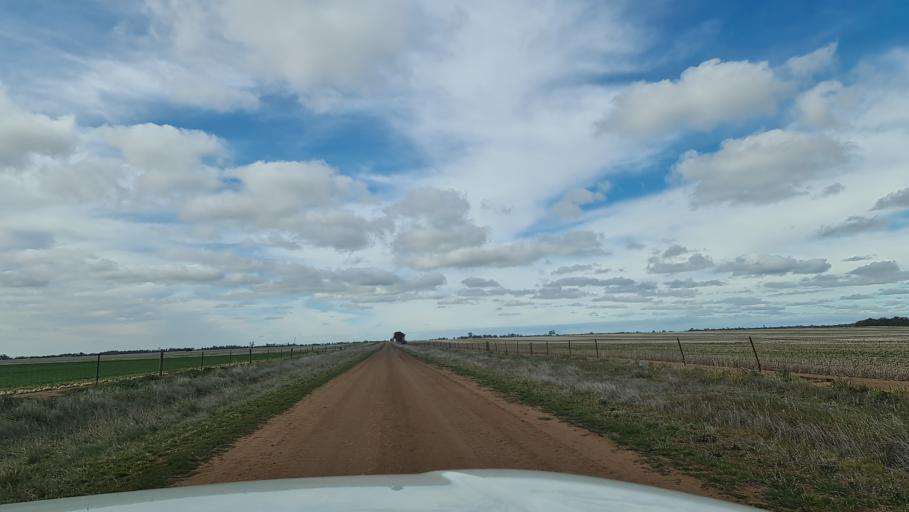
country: AU
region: Victoria
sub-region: Horsham
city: Horsham
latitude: -36.6313
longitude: 142.4213
